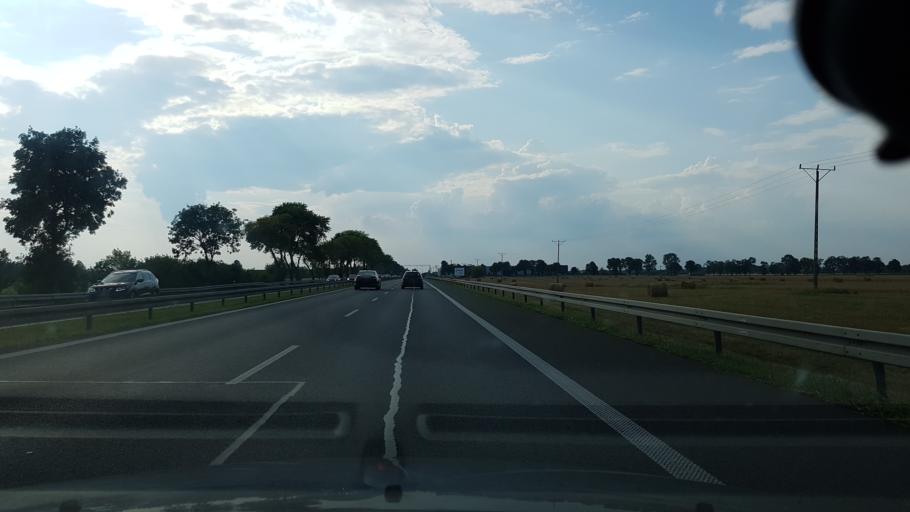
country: PL
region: Masovian Voivodeship
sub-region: Powiat warszawski zachodni
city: Dziekanow Lesny
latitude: 52.3684
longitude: 20.8022
